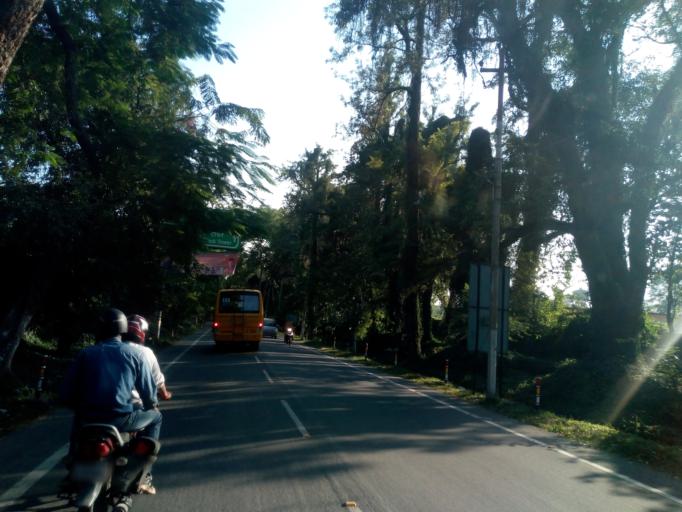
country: IN
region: Uttarakhand
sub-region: Dehradun
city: Dehradun
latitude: 30.3519
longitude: 78.0435
